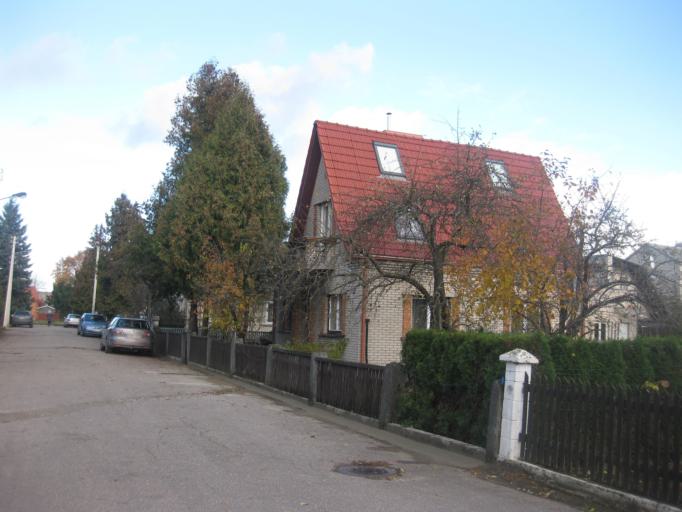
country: LT
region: Kauno apskritis
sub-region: Kaunas
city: Silainiai
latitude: 54.9174
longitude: 23.8981
